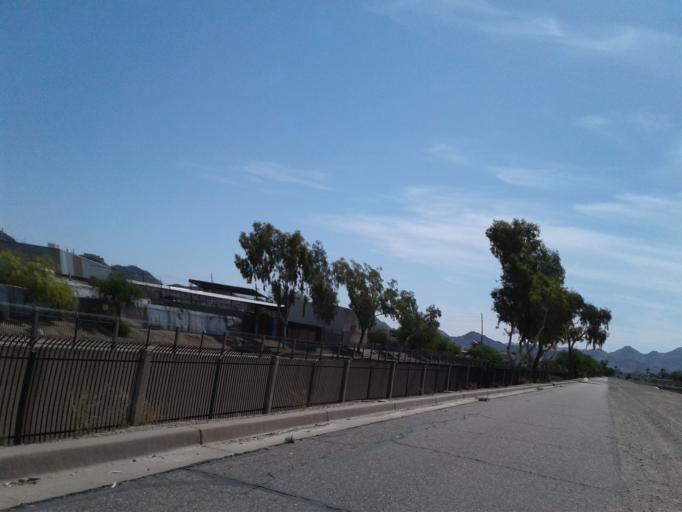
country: US
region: Arizona
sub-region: Maricopa County
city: Glendale
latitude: 33.5701
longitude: -112.0927
